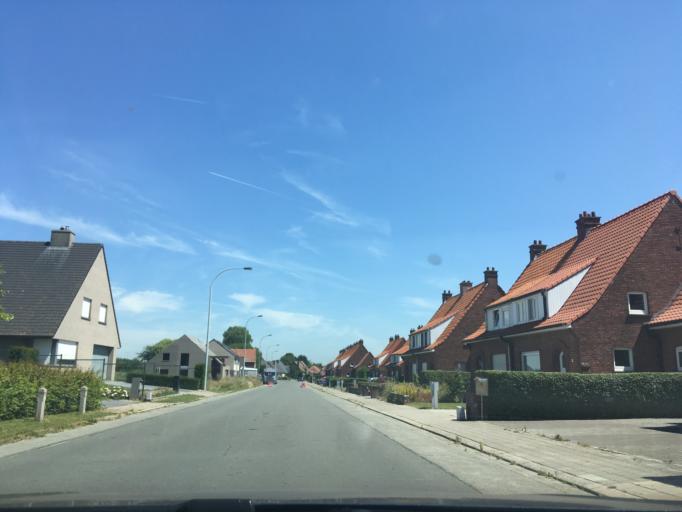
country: BE
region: Flanders
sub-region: Provincie West-Vlaanderen
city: Tielt
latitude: 51.0038
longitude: 3.3135
